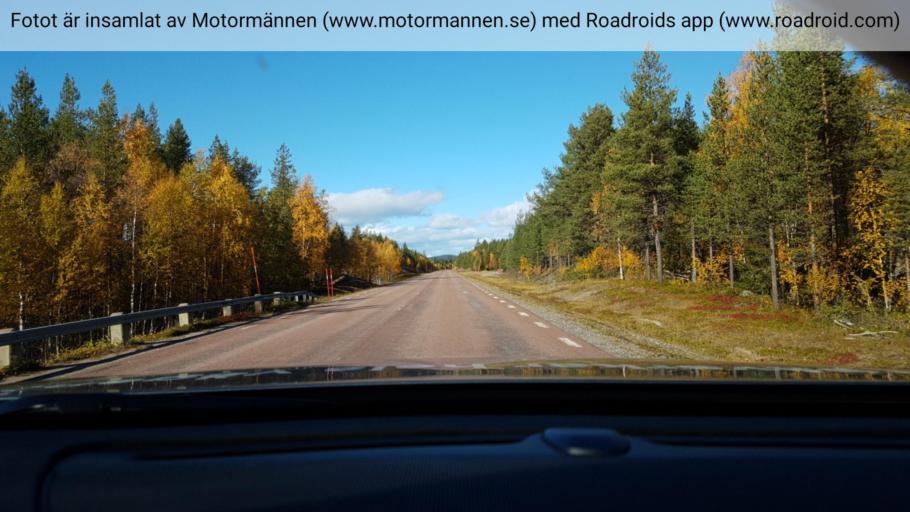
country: SE
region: Norrbotten
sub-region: Arjeplogs Kommun
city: Arjeplog
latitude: 66.0072
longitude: 18.1044
